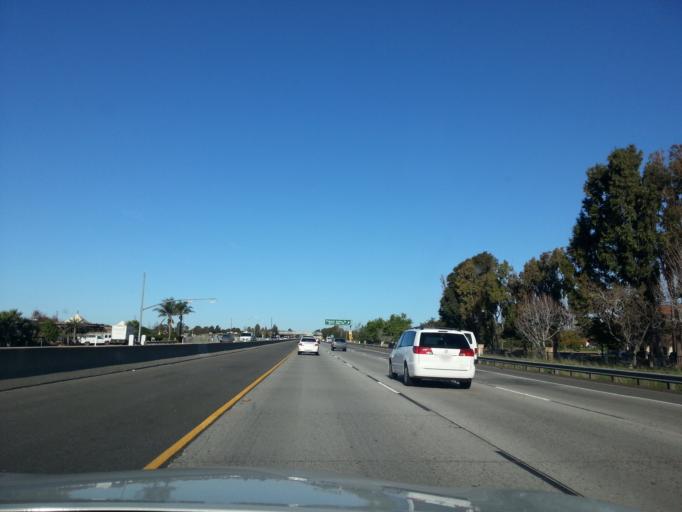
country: US
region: California
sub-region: Ventura County
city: Camarillo
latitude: 34.2116
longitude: -119.0012
